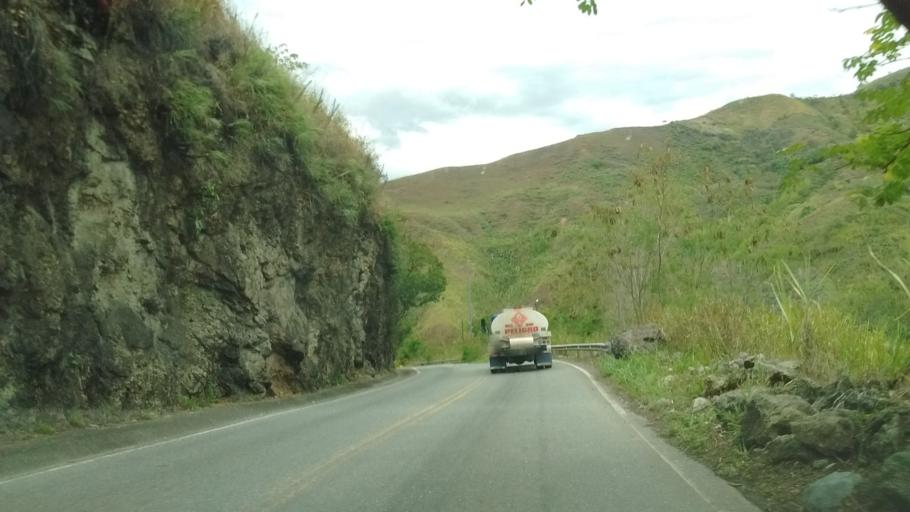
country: CO
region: Cauca
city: La Sierra
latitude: 2.1985
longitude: -76.8228
